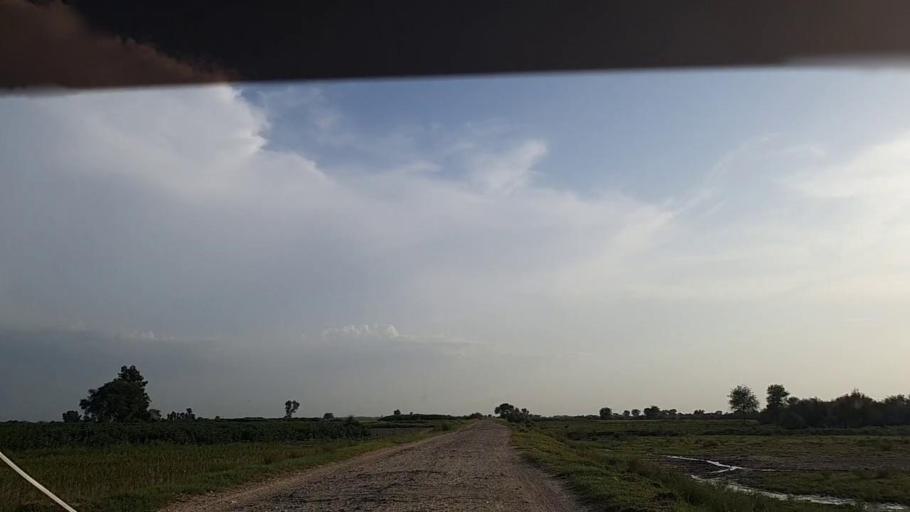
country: PK
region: Sindh
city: Khanpur
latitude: 27.8064
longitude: 69.3179
